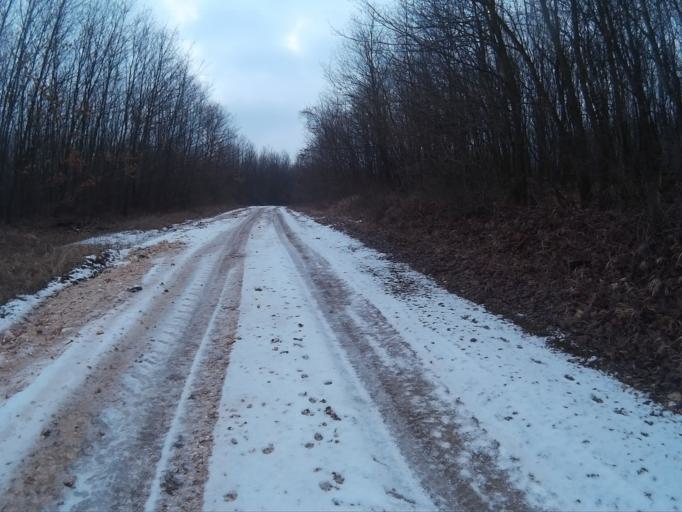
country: HU
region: Komarom-Esztergom
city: Tarjan
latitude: 47.5825
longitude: 18.5268
